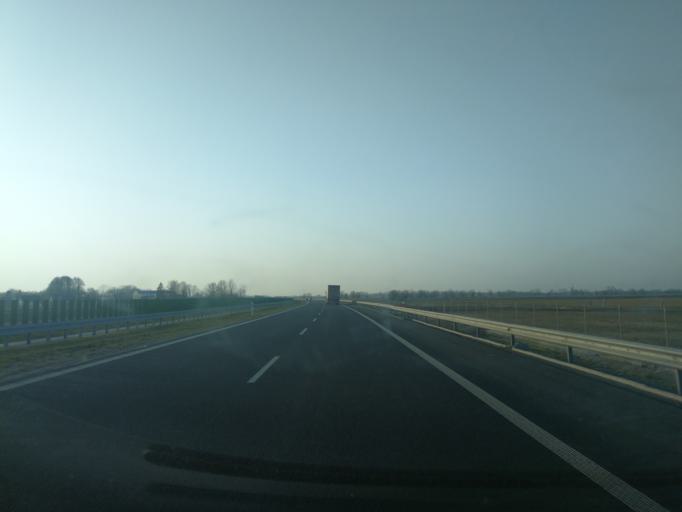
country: PL
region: Pomeranian Voivodeship
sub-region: Powiat nowodworski
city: Nowy Dwor Gdanski
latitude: 54.1887
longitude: 19.1666
